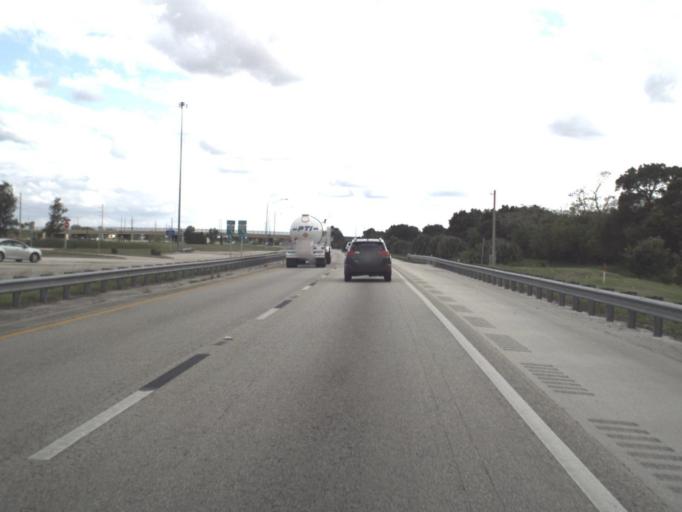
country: US
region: Florida
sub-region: Saint Lucie County
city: Port Saint Lucie
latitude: 27.3015
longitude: -80.3737
